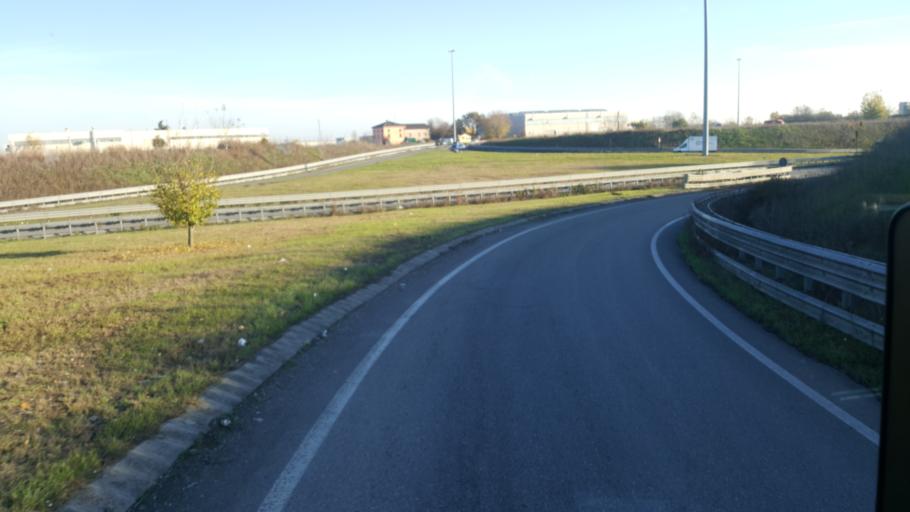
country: IT
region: Emilia-Romagna
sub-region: Provincia di Parma
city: Ponte Taro
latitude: 44.8337
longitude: 10.2196
